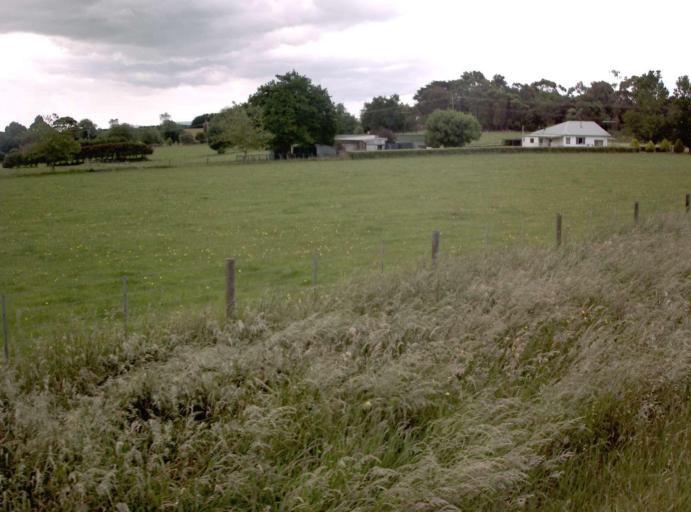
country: AU
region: Victoria
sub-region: Baw Baw
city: Warragul
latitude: -38.1018
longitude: 145.9226
